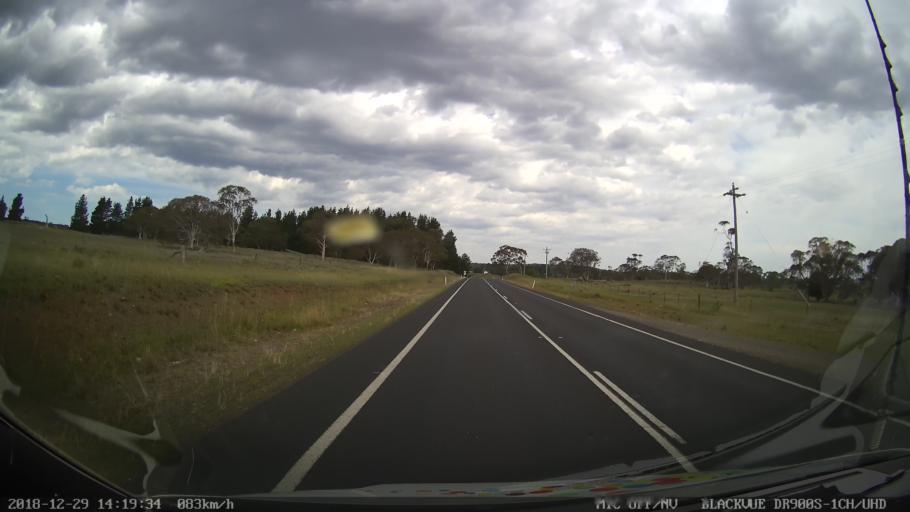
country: AU
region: New South Wales
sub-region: Cooma-Monaro
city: Cooma
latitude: -36.5001
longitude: 149.2818
